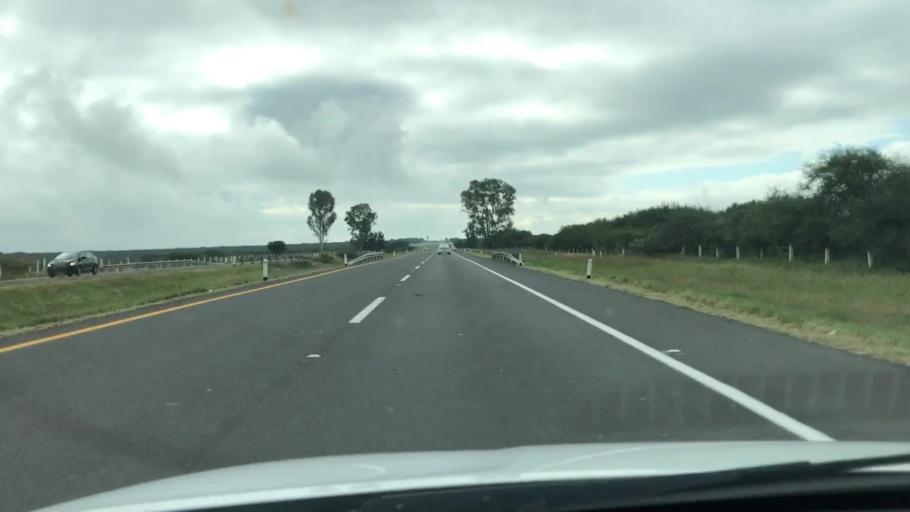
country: MX
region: Jalisco
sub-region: Lagos de Moreno
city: Cristeros [Fraccionamiento]
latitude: 21.2452
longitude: -101.9427
